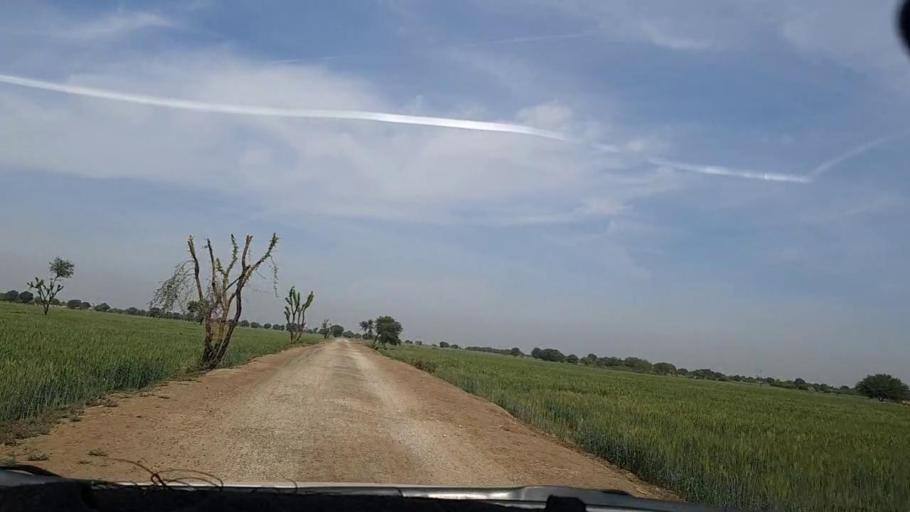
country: PK
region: Sindh
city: Dhoro Naro
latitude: 25.4434
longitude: 69.4971
